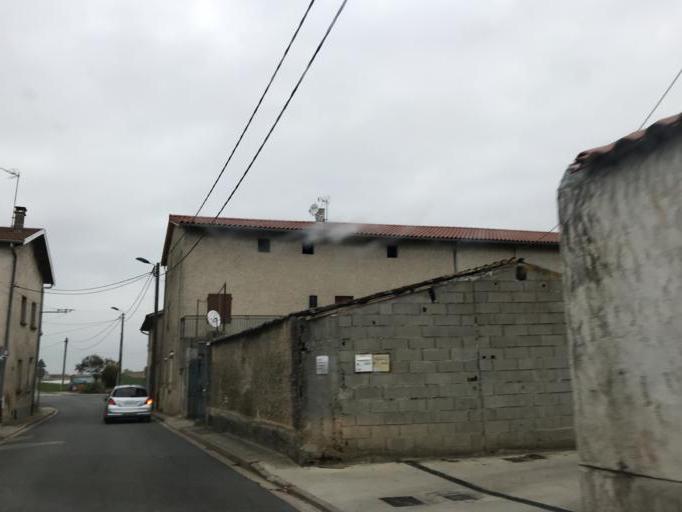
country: FR
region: Rhone-Alpes
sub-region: Departement de l'Ain
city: Miribel
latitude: 45.8321
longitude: 4.9470
